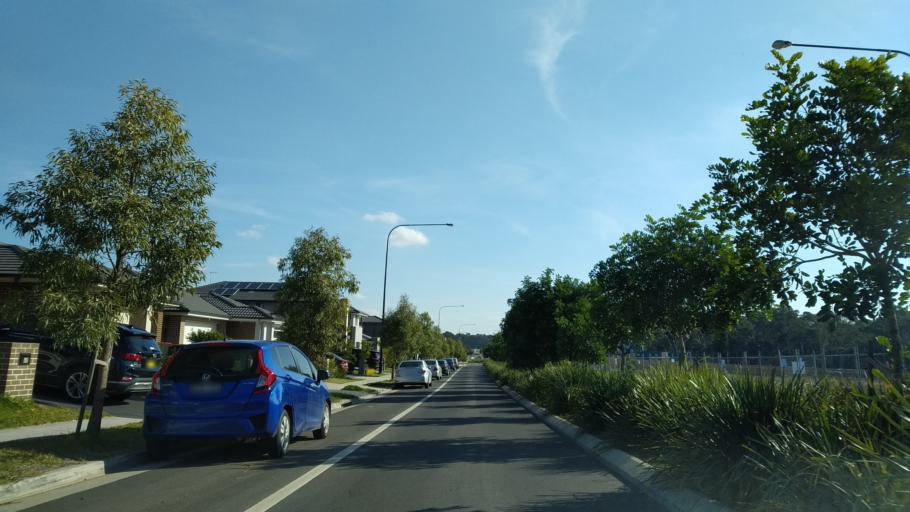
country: AU
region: New South Wales
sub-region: Blacktown
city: Hassall Grove
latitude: -33.7229
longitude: 150.8508
